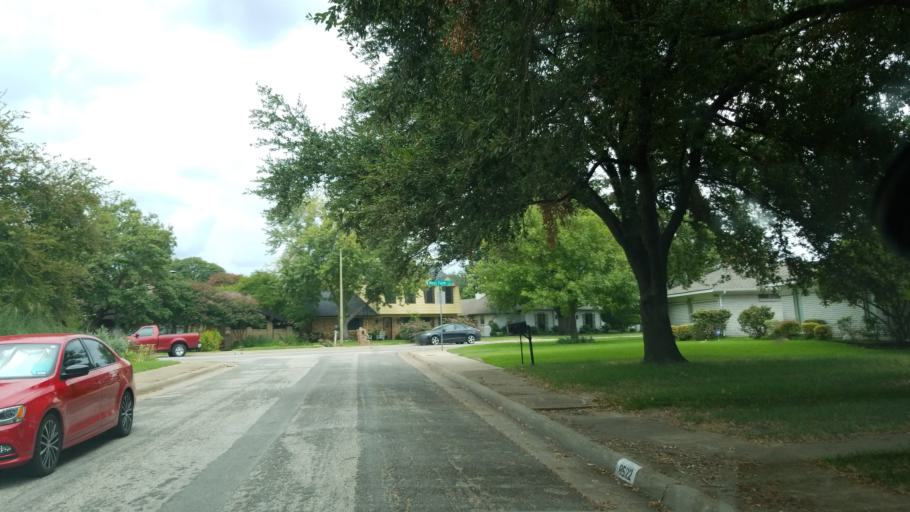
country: US
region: Texas
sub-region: Dallas County
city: Richardson
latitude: 32.8957
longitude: -96.7404
